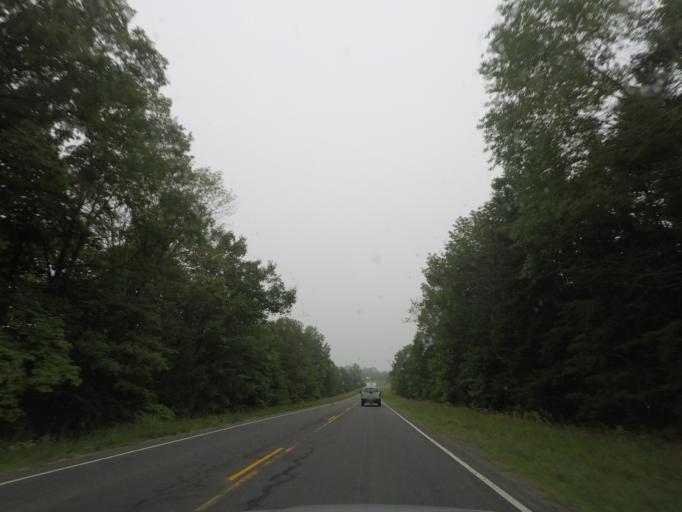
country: US
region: Virginia
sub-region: Buckingham County
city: Buckingham
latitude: 37.5167
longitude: -78.4933
